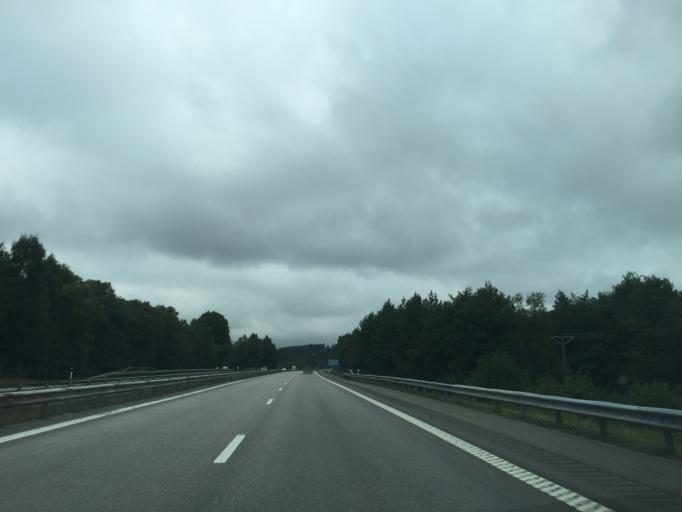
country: SE
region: Halland
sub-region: Kungsbacka Kommun
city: Frillesas
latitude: 57.3787
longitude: 12.1965
